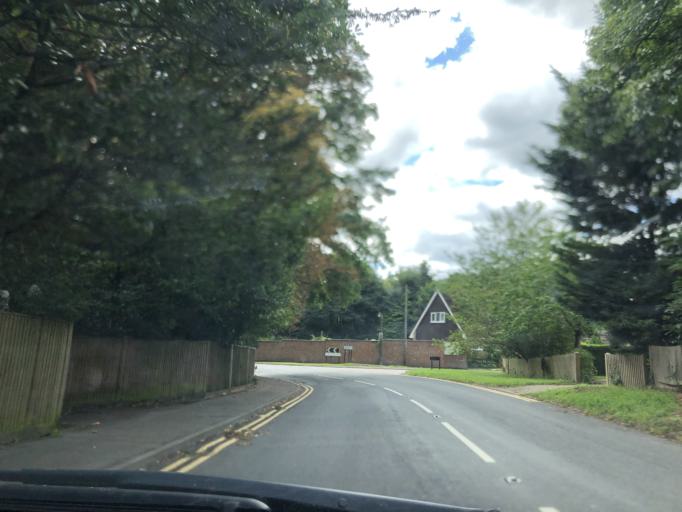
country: GB
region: England
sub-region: Kent
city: Halstead
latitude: 51.2796
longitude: 0.1269
